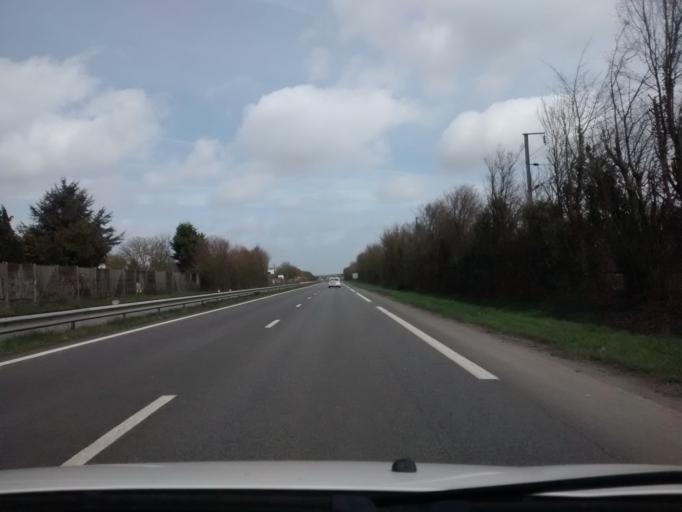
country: FR
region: Brittany
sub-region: Departement d'Ille-et-Vilaine
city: Saint-Jacques-de-la-Lande
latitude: 48.0611
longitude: -1.7208
